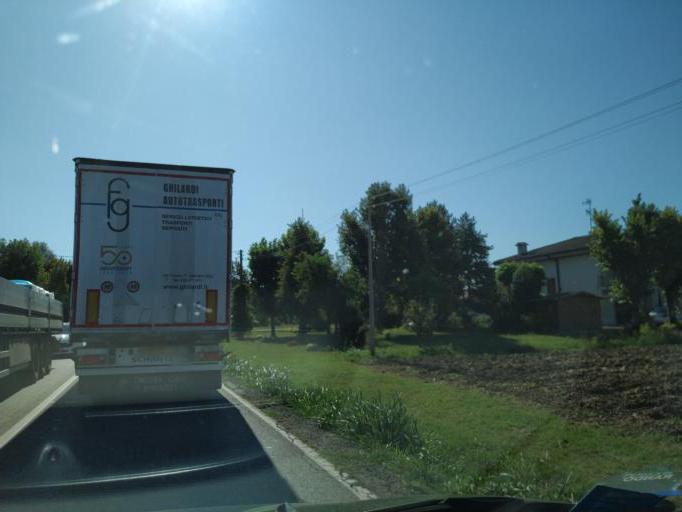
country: IT
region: Emilia-Romagna
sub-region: Provincia di Bologna
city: San Giovanni in Persiceto
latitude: 44.6464
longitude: 11.1682
